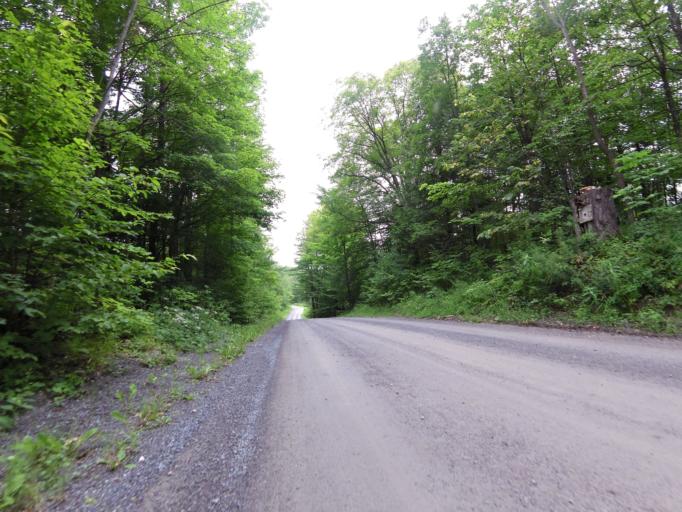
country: CA
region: Ontario
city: Kingston
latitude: 44.5704
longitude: -76.5477
